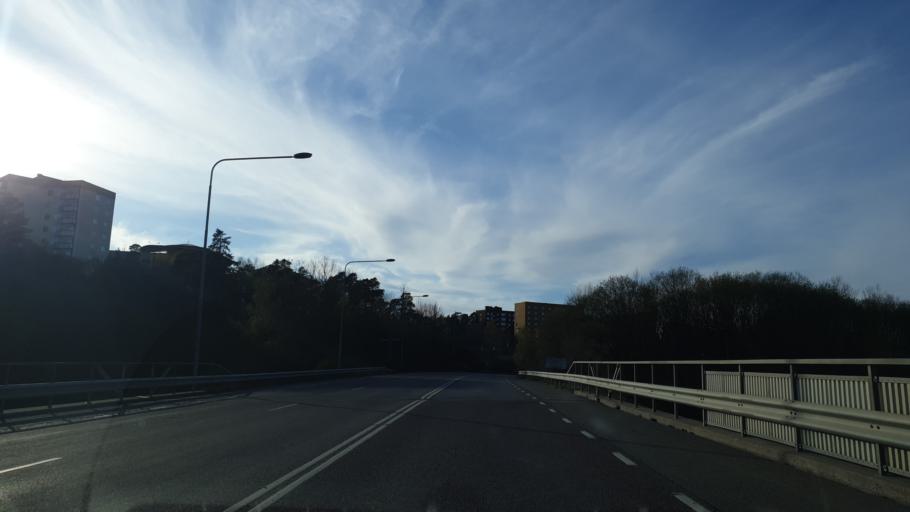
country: SE
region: Stockholm
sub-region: Solna Kommun
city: Solna
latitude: 59.3476
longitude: 18.0085
